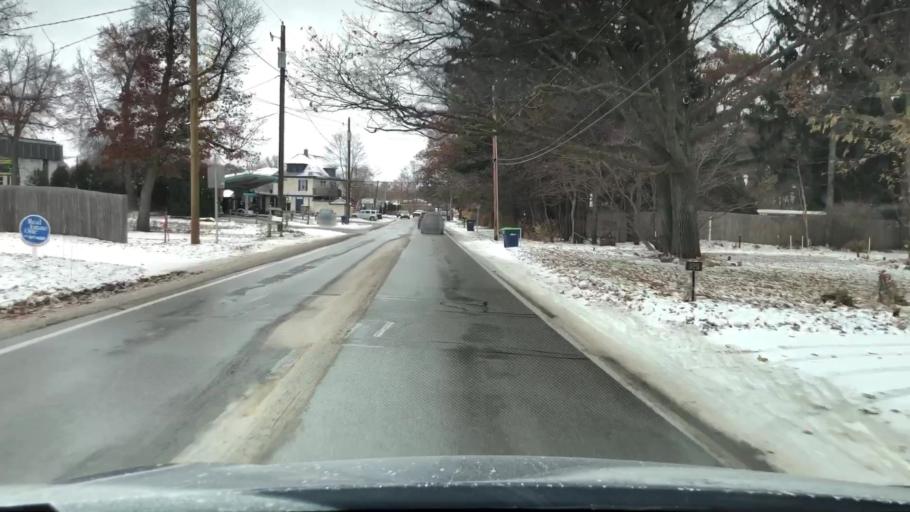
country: US
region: Michigan
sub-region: Grand Traverse County
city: Traverse City
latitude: 44.7649
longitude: -85.5992
